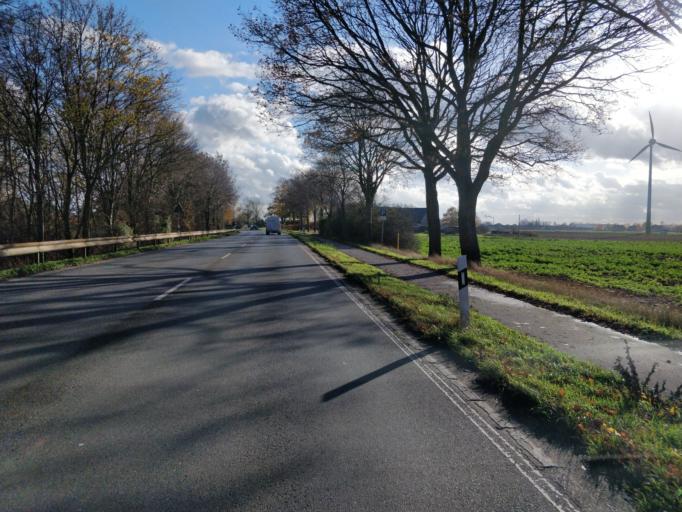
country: DE
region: North Rhine-Westphalia
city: Rees
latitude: 51.7809
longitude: 6.3766
